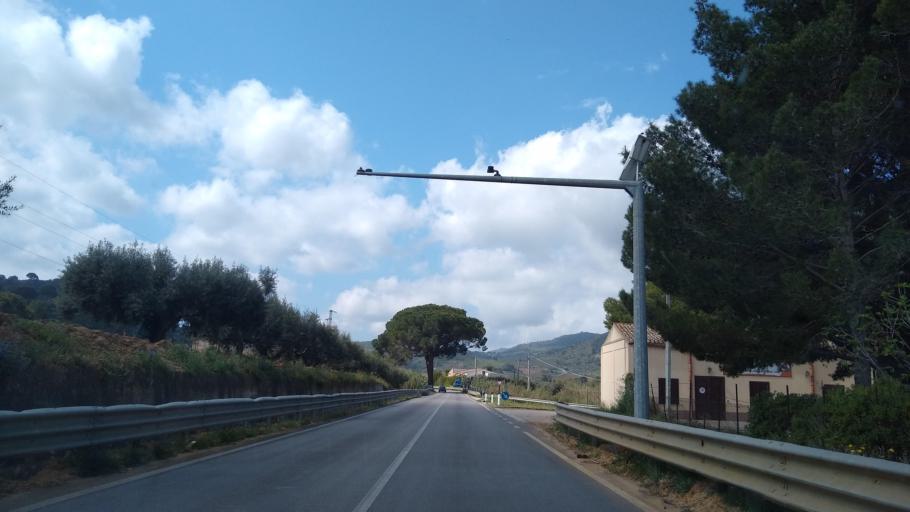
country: IT
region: Sicily
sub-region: Trapani
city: Calatafimi
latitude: 37.9413
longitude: 12.8570
